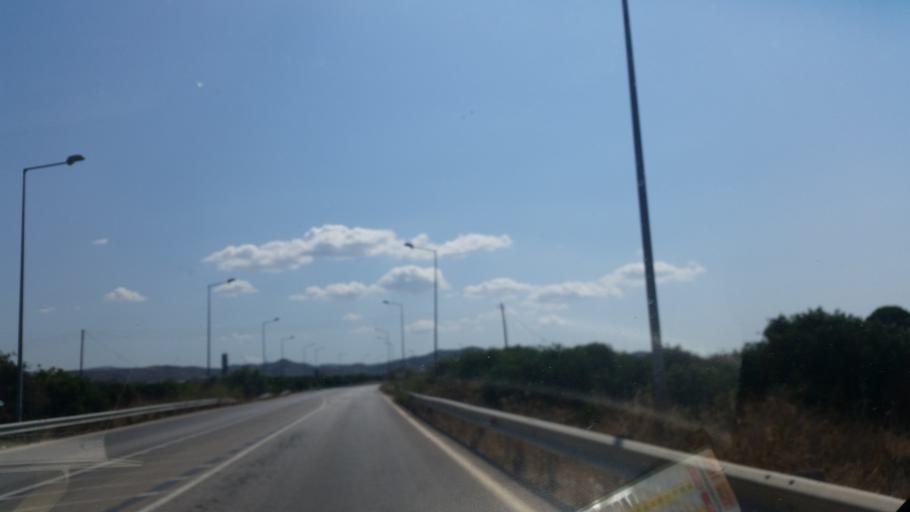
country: GR
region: Peloponnese
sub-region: Nomos Argolidos
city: Ayia Trias
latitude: 37.6427
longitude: 22.8121
